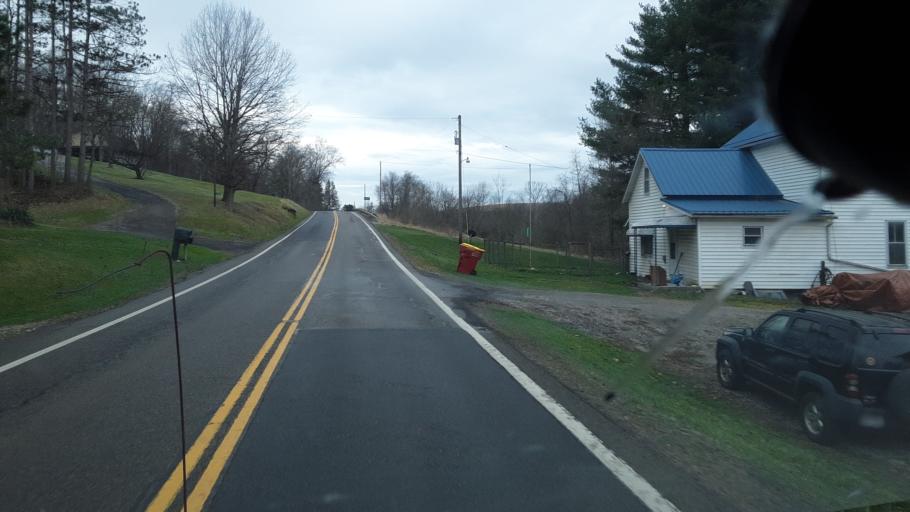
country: US
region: Ohio
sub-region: Coshocton County
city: West Lafayette
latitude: 40.3363
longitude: -81.7394
